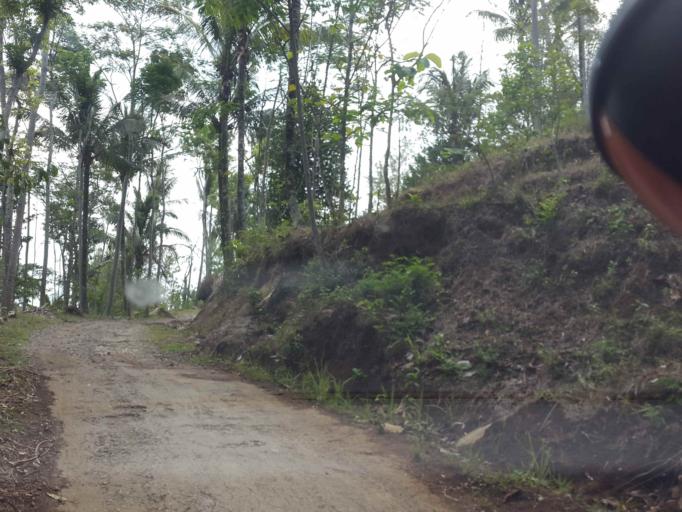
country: ID
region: East Java
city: Krajan
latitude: -8.2342
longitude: 111.1447
